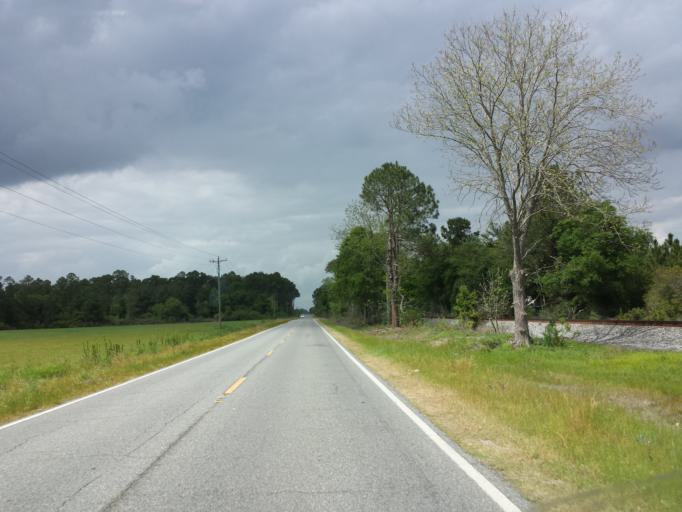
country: US
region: Georgia
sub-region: Tift County
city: Omega
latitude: 31.3000
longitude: -83.4715
